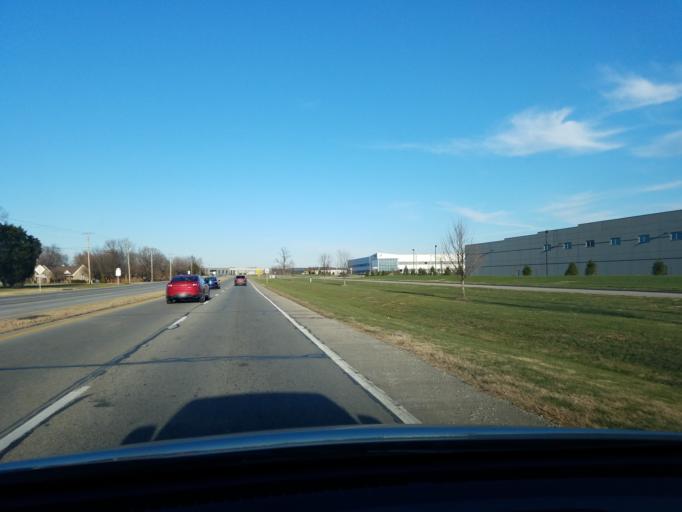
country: US
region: Indiana
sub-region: Clark County
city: Sellersburg
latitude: 38.3840
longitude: -85.6866
